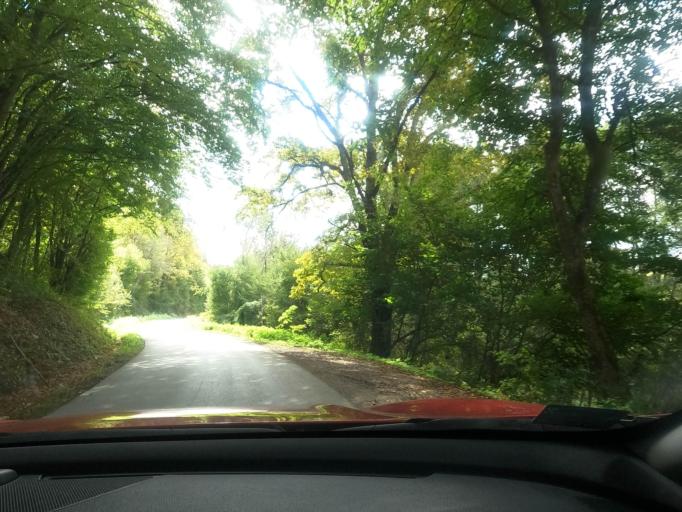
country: BA
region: Federation of Bosnia and Herzegovina
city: Velika Kladusa
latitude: 45.2351
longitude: 15.7368
